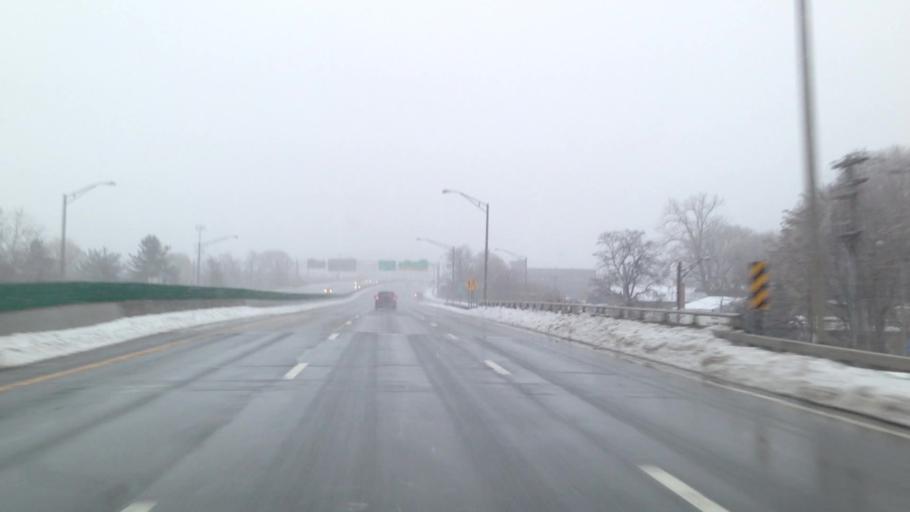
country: US
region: New York
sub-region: Onondaga County
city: Syracuse
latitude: 43.0559
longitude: -76.1710
